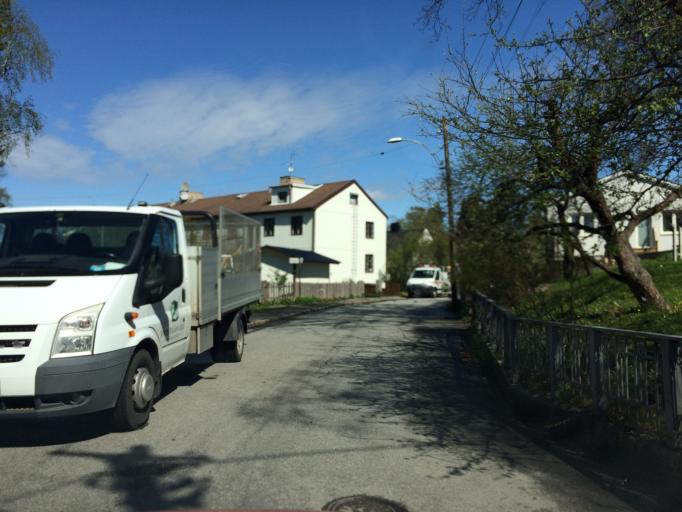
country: SE
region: Stockholm
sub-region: Huddinge Kommun
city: Segeltorp
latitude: 59.2934
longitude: 17.9599
